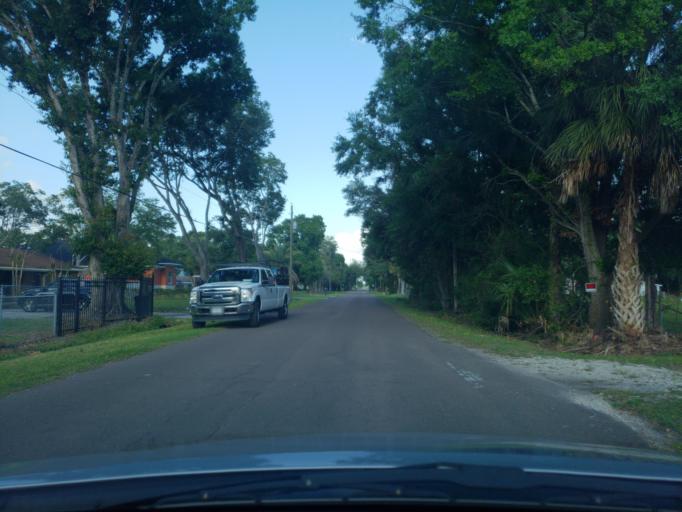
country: US
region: Florida
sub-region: Hillsborough County
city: Palm River-Clair Mel
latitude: 27.9155
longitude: -82.3869
